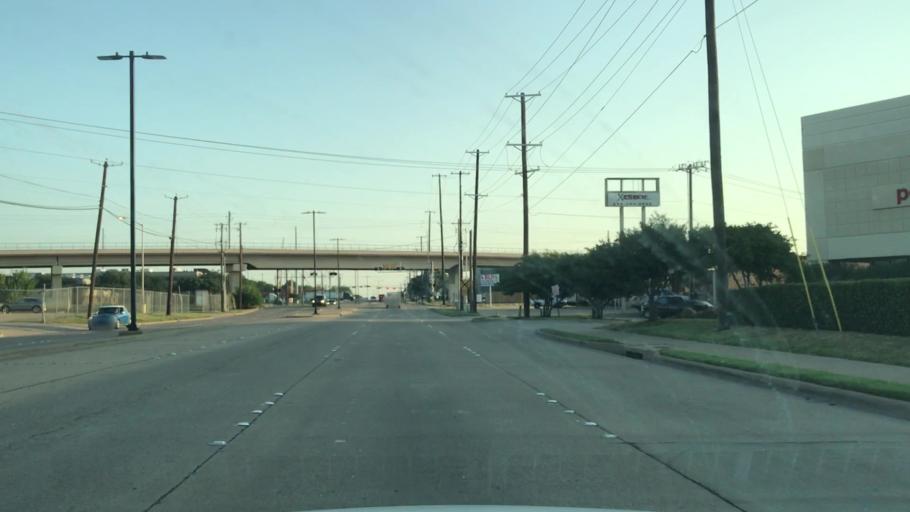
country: US
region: Texas
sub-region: Dallas County
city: Garland
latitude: 32.9056
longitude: -96.6828
